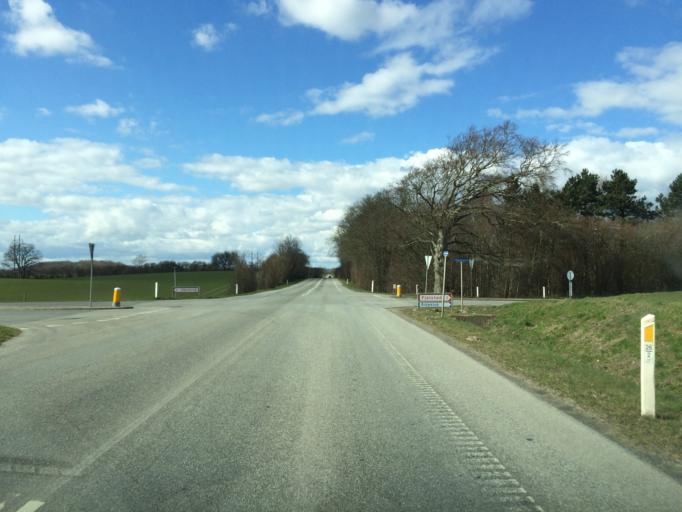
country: DK
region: South Denmark
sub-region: Middelfart Kommune
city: Brenderup
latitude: 55.4337
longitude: 10.0074
